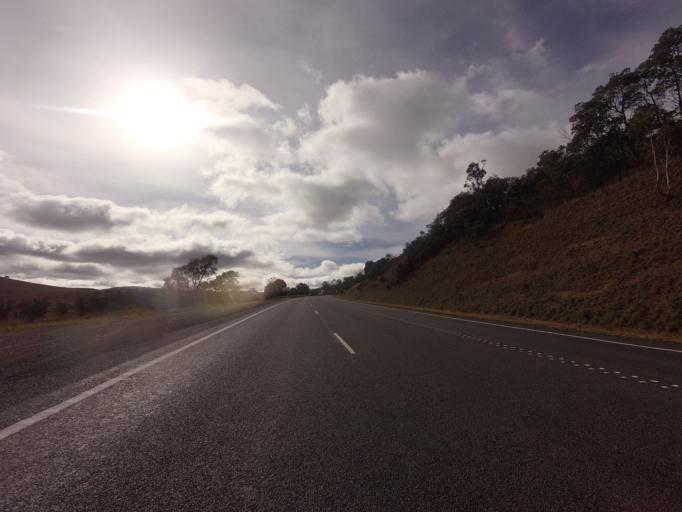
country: AU
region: Tasmania
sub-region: Brighton
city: Bridgewater
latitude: -42.4141
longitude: 147.2618
